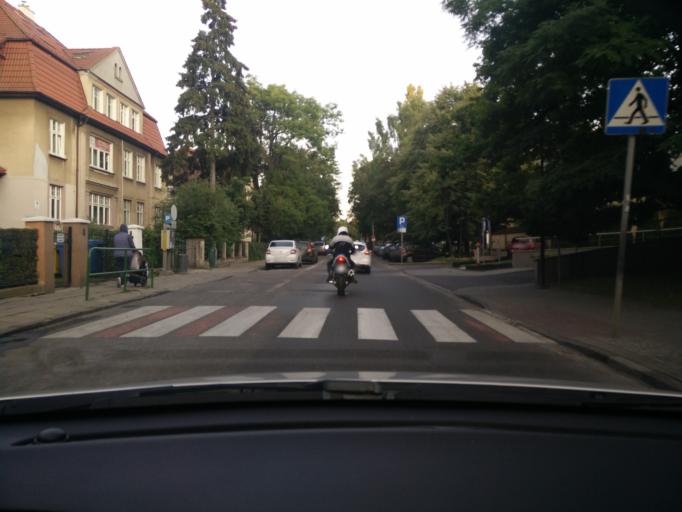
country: PL
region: Pomeranian Voivodeship
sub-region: Sopot
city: Sopot
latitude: 54.4509
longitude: 18.5618
